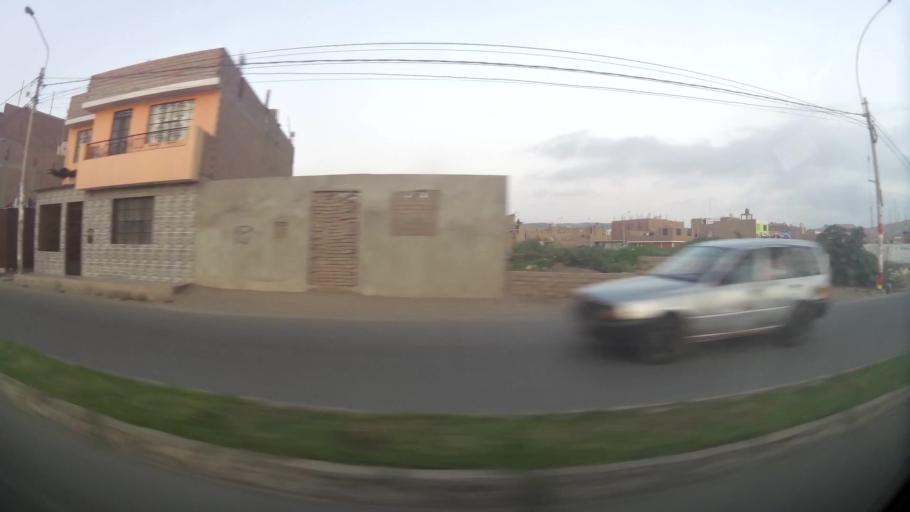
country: PE
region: Lima
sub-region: Huaura
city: Huacho
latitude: -11.1194
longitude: -77.6061
